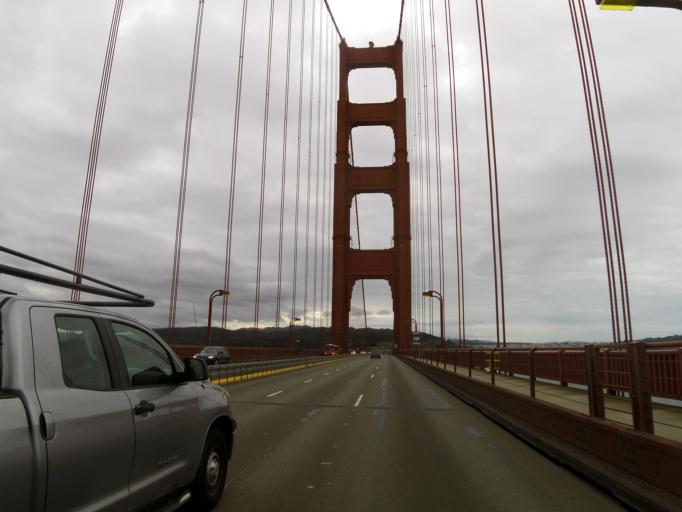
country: US
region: California
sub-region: Marin County
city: Sausalito
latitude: 37.8159
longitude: -122.4787
